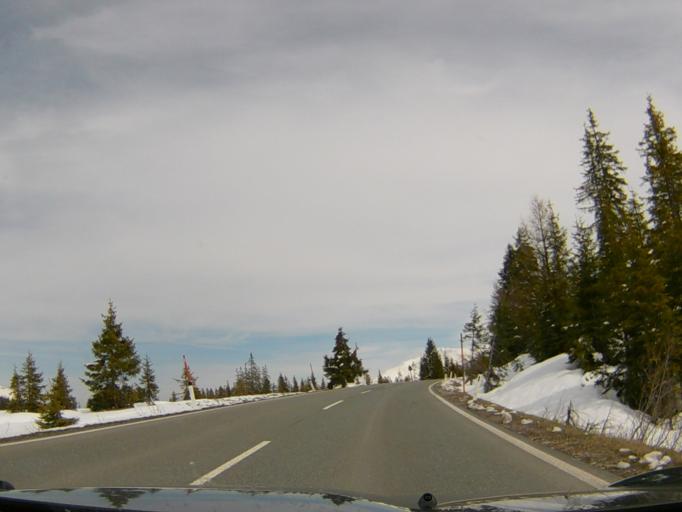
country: AT
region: Salzburg
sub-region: Politischer Bezirk Zell am See
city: Krimml
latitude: 47.2418
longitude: 12.1409
